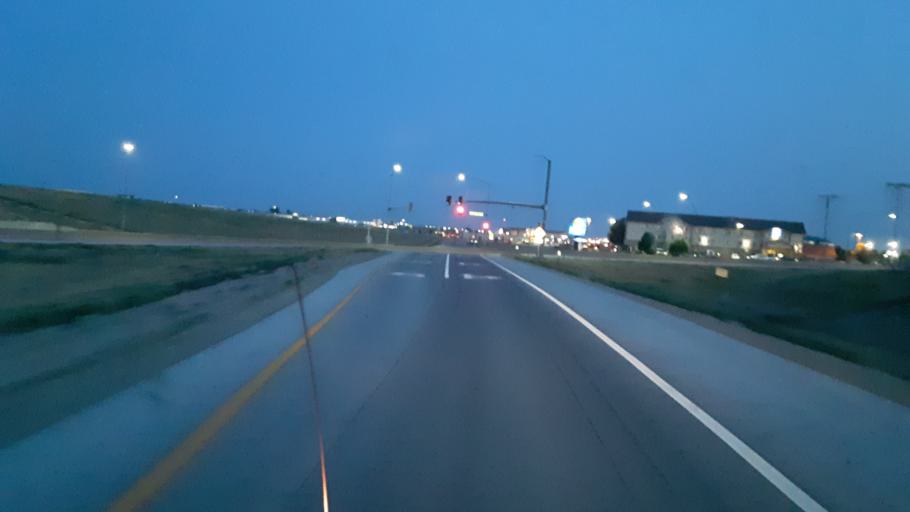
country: US
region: Kansas
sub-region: Finney County
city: Garden City
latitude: 37.9829
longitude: -100.8393
